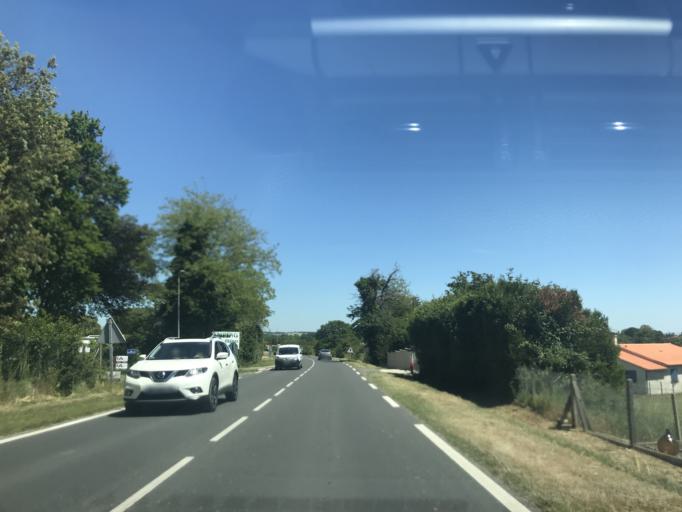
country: FR
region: Poitou-Charentes
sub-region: Departement de la Charente-Maritime
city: Meschers-sur-Gironde
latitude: 45.5652
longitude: -0.9598
